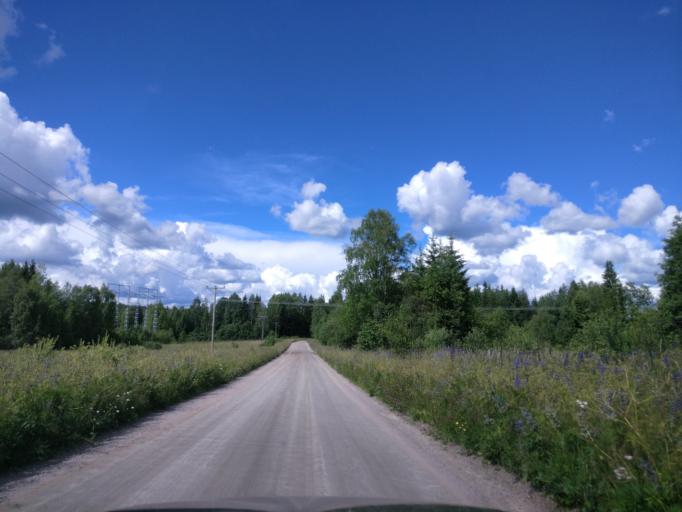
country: SE
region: Vaermland
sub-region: Hagfors Kommun
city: Hagfors
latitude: 60.0312
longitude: 13.6686
